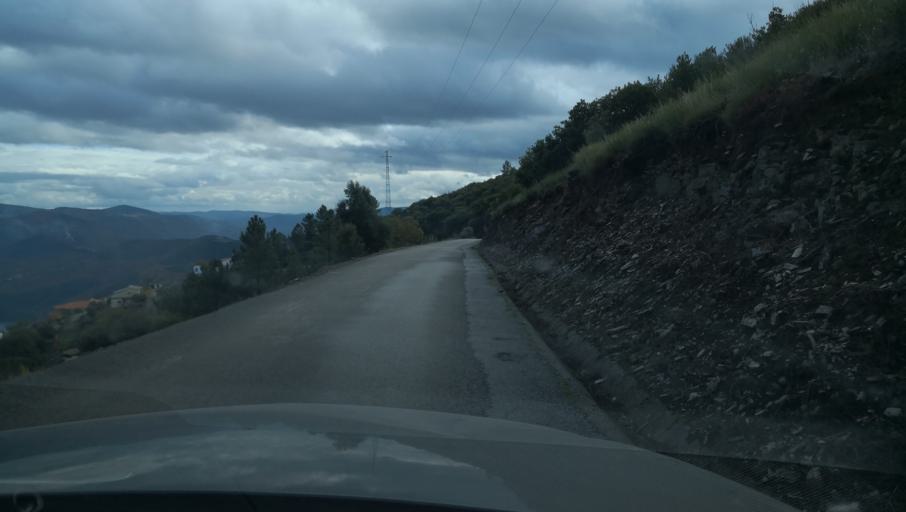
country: PT
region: Vila Real
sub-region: Sabrosa
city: Vilela
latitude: 41.1934
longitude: -7.5715
